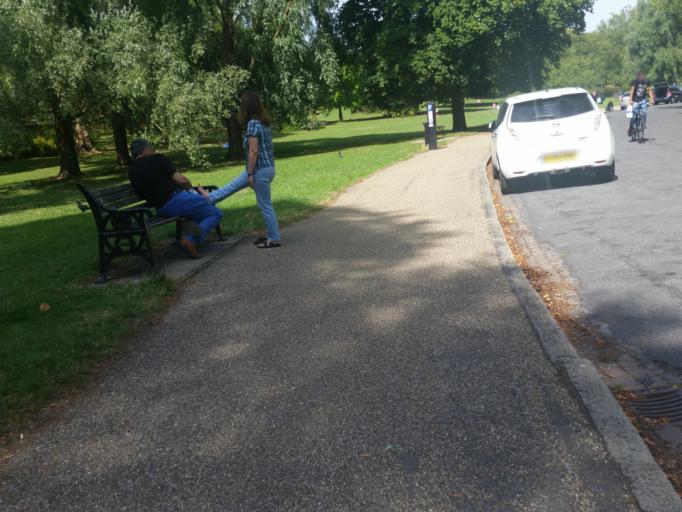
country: GB
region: England
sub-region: Greater London
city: Harringay
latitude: 51.5730
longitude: -0.1040
